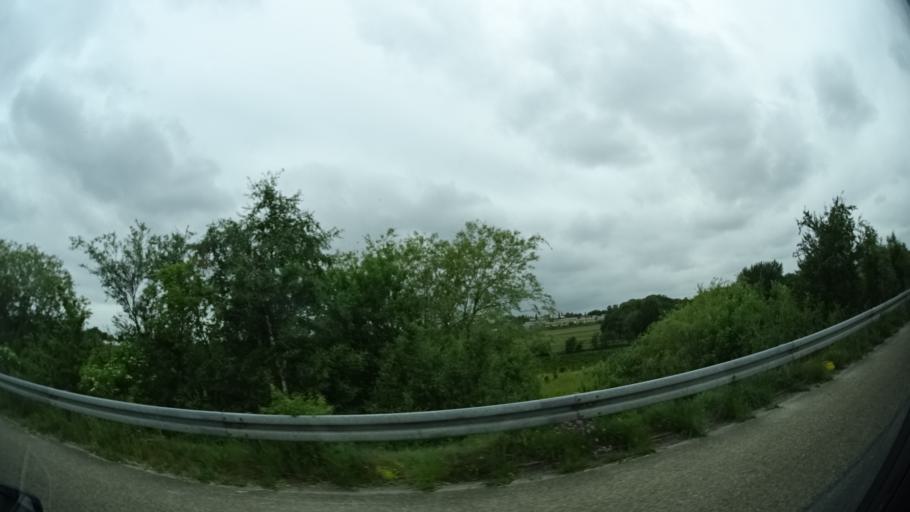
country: DK
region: Central Jutland
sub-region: Arhus Kommune
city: Logten
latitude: 56.2771
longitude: 10.3313
